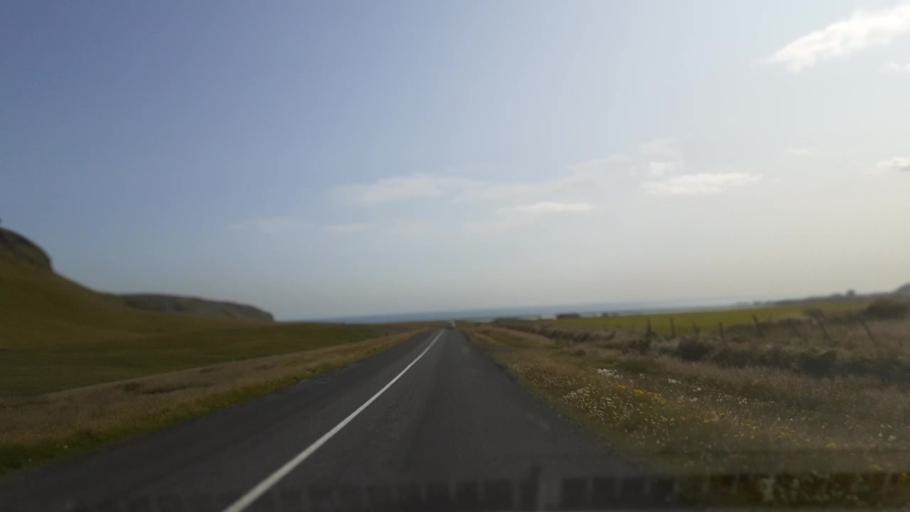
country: IS
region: South
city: Vestmannaeyjar
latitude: 63.4418
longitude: -19.0597
